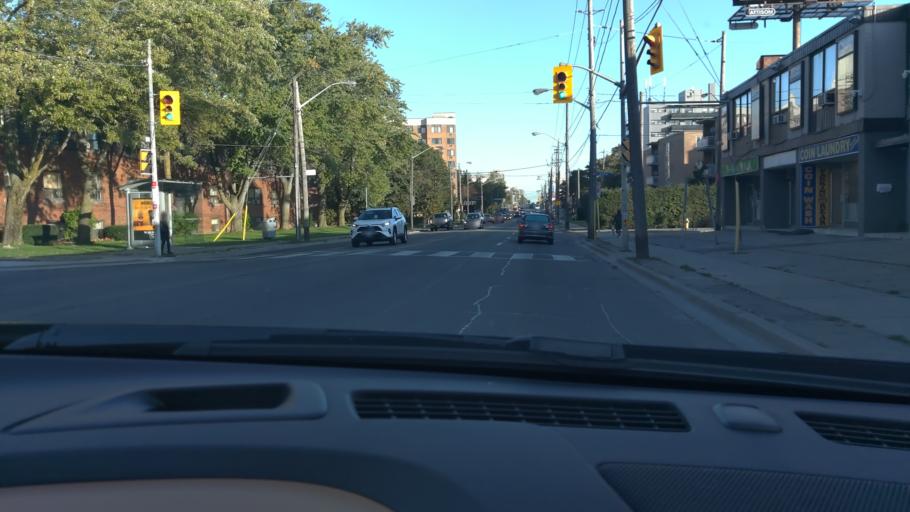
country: CA
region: Ontario
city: Toronto
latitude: 43.7229
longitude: -79.4305
